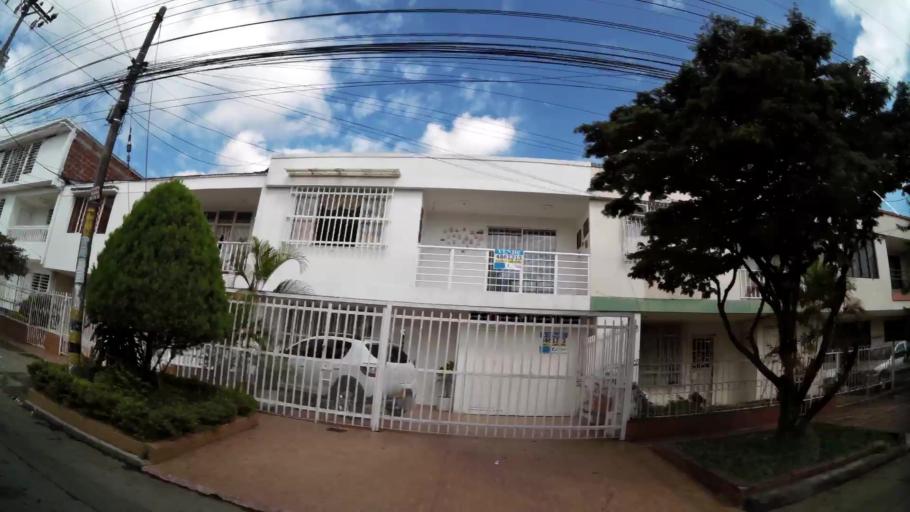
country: CO
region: Valle del Cauca
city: Cali
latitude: 3.4261
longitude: -76.5423
